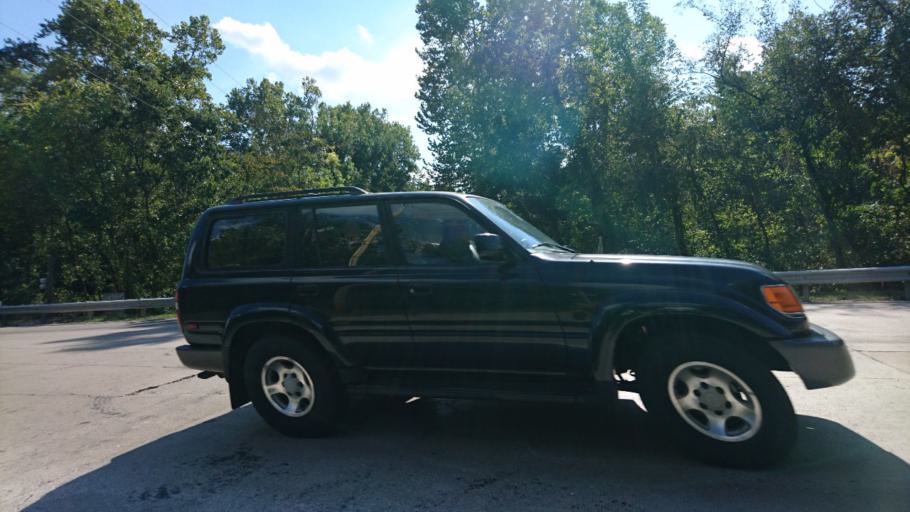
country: US
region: Missouri
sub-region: Saint Louis County
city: Wildwood
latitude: 38.5564
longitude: -90.6429
